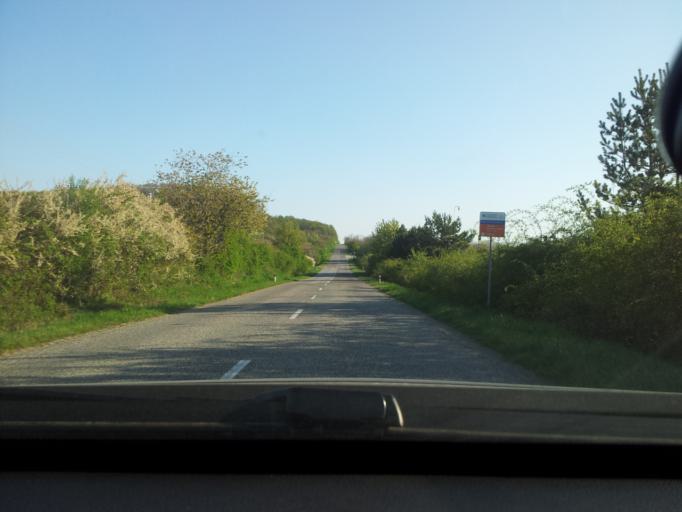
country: SK
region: Nitriansky
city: Tlmace
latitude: 48.2686
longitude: 18.4462
